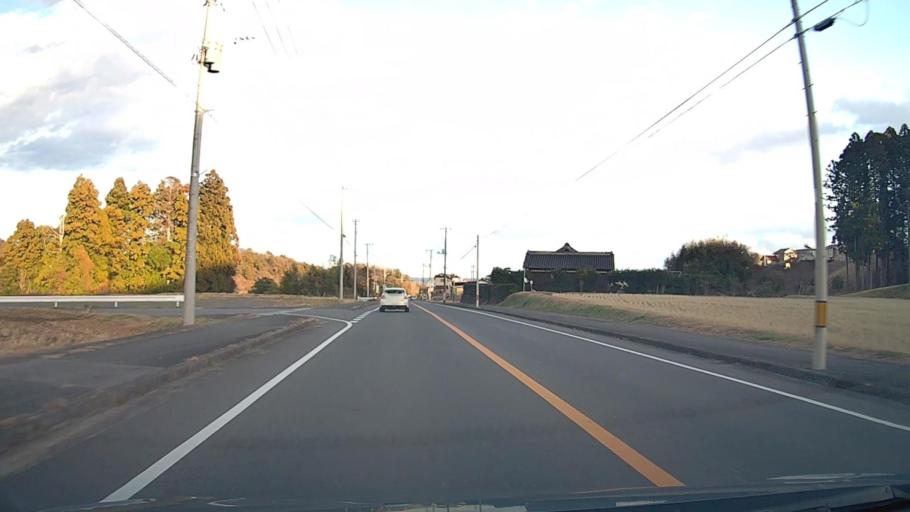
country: JP
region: Ibaraki
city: Kitaibaraki
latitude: 36.8057
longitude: 140.7527
